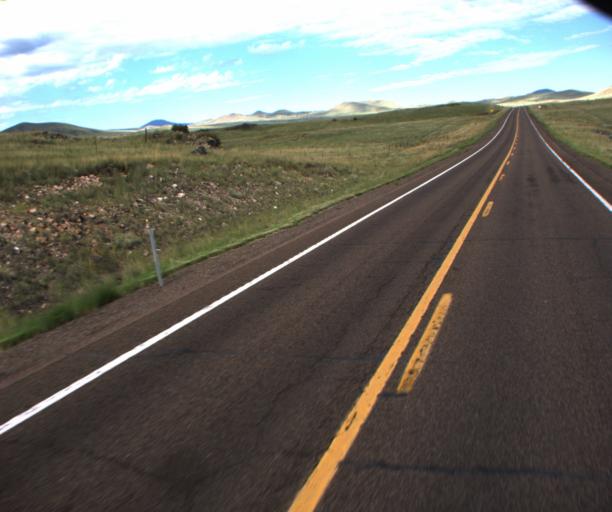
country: US
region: Arizona
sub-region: Apache County
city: Springerville
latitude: 34.1958
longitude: -109.3782
